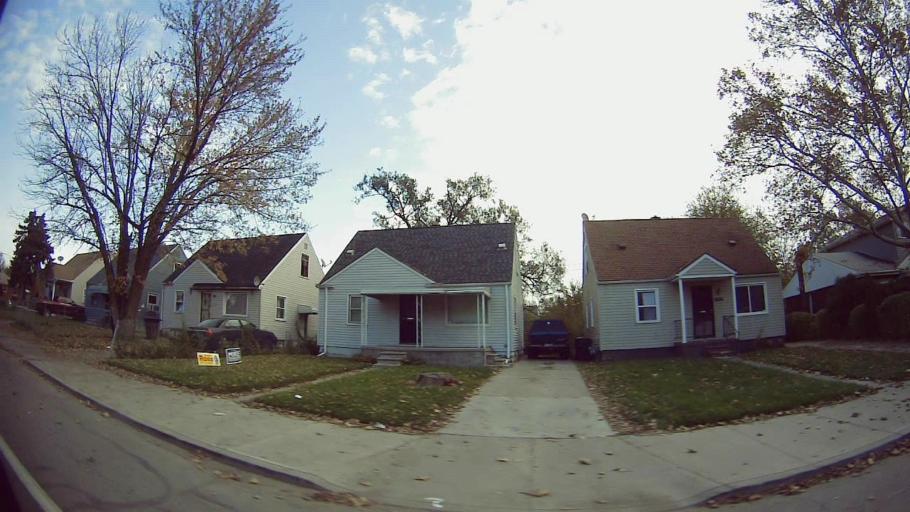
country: US
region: Michigan
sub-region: Wayne County
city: Dearborn
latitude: 42.3673
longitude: -83.1777
